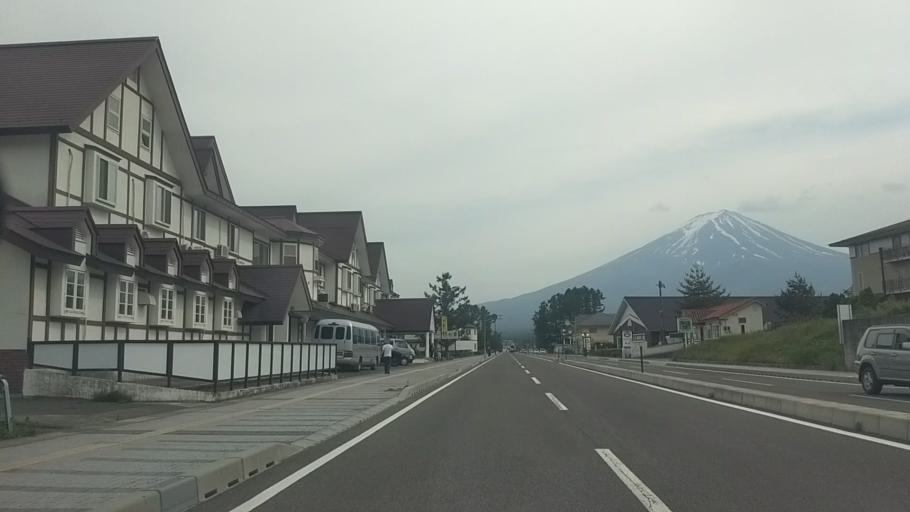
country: JP
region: Yamanashi
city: Fujikawaguchiko
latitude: 35.4978
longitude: 138.7560
